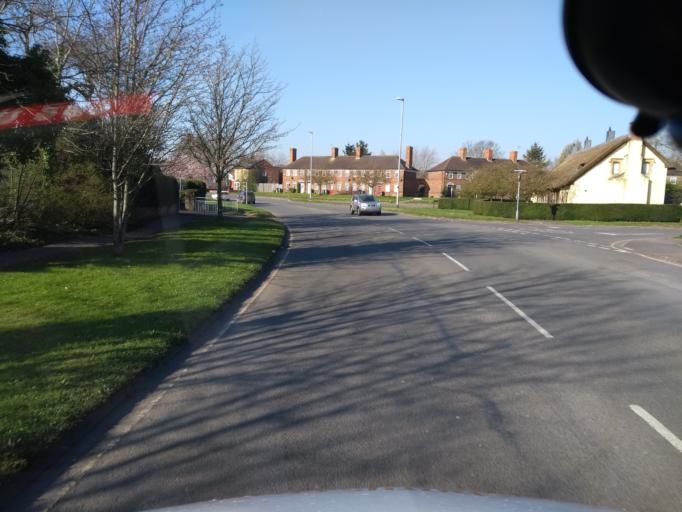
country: GB
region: England
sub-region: Somerset
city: Taunton
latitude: 51.0176
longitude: -3.0863
